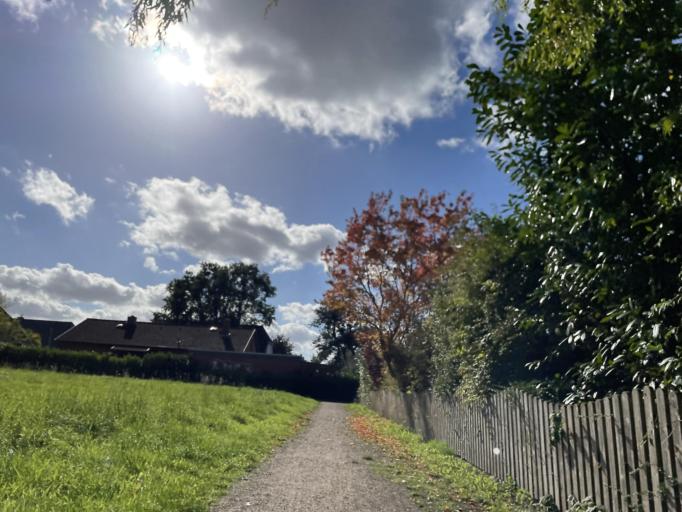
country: DE
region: Lower Saxony
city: Barendorf
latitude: 53.2321
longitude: 10.5185
